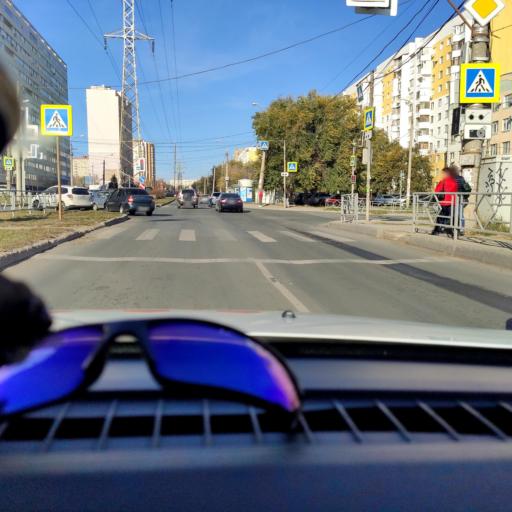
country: RU
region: Samara
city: Samara
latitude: 53.2061
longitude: 50.2137
